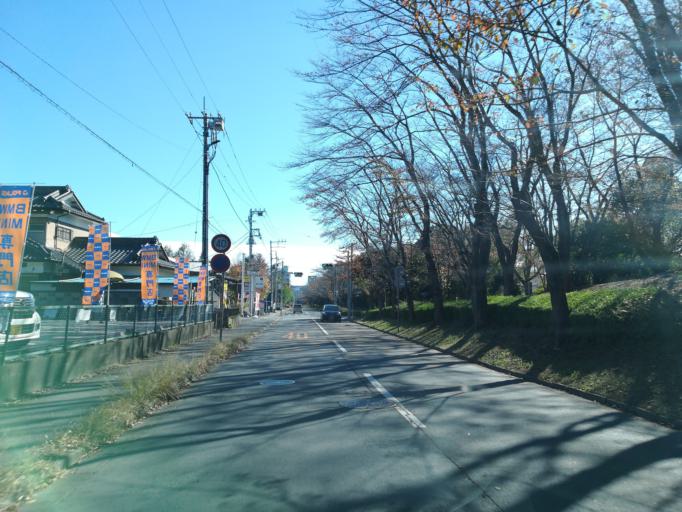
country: JP
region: Ibaraki
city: Naka
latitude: 36.0988
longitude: 140.1058
